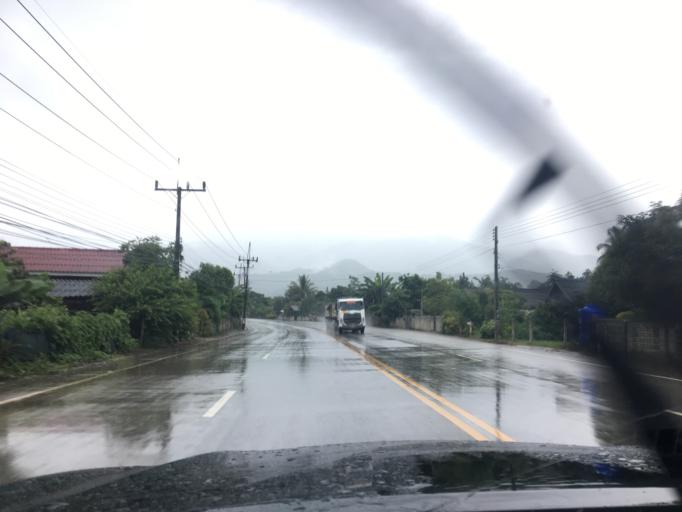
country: TH
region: Chiang Rai
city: Chiang Khong
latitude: 20.3010
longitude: 100.2482
